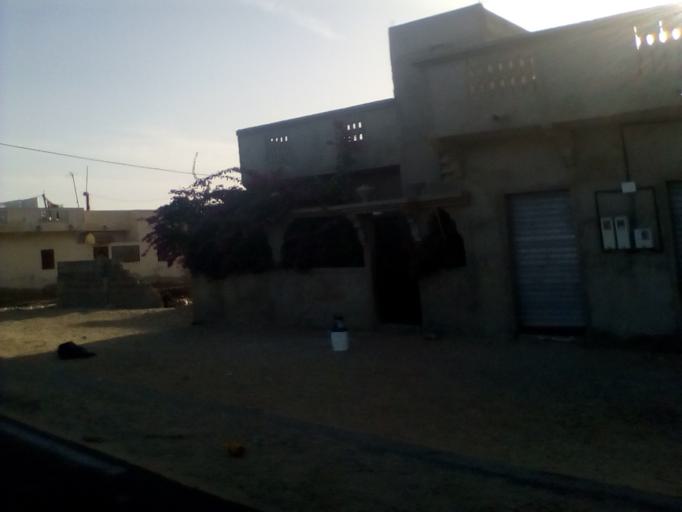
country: SN
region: Saint-Louis
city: Saint-Louis
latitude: 15.9979
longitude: -16.4837
